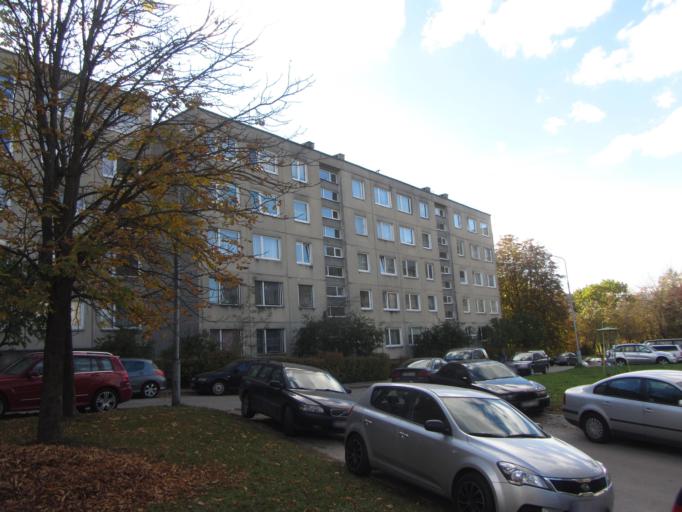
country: LT
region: Vilnius County
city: Lazdynai
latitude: 54.6735
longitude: 25.2044
